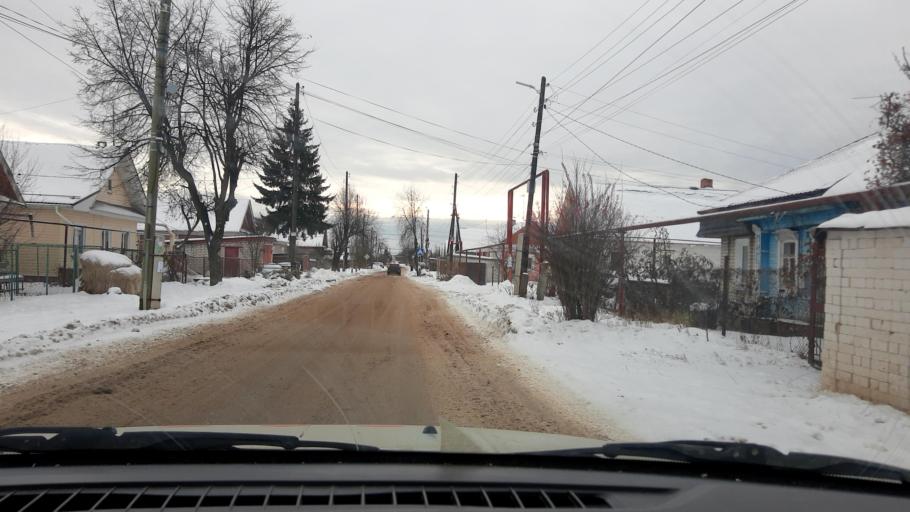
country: RU
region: Nizjnij Novgorod
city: Gorodets
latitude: 56.6669
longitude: 43.4775
